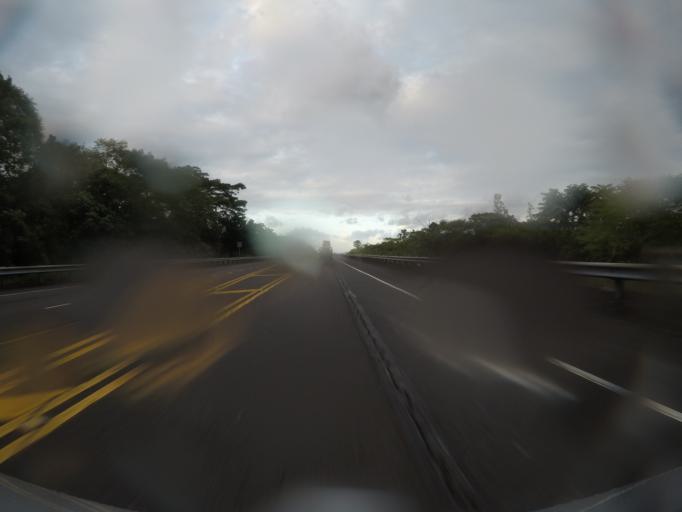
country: US
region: Hawaii
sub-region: Hawaii County
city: Hilo
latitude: 19.6926
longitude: -155.1096
